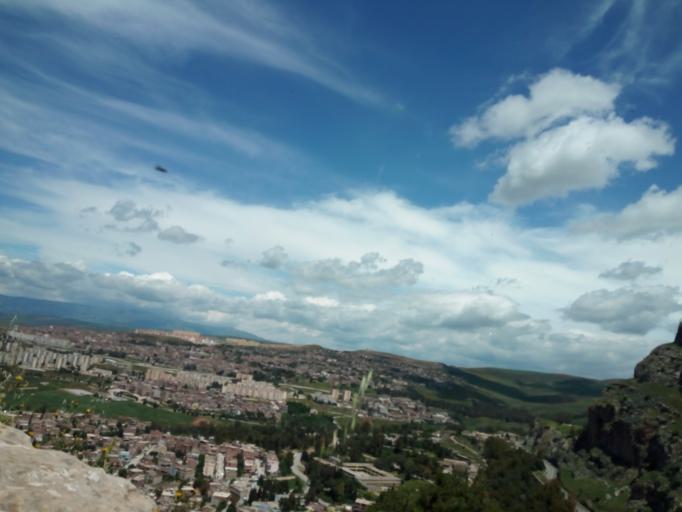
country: DZ
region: Constantine
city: Constantine
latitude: 36.3753
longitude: 6.6142
